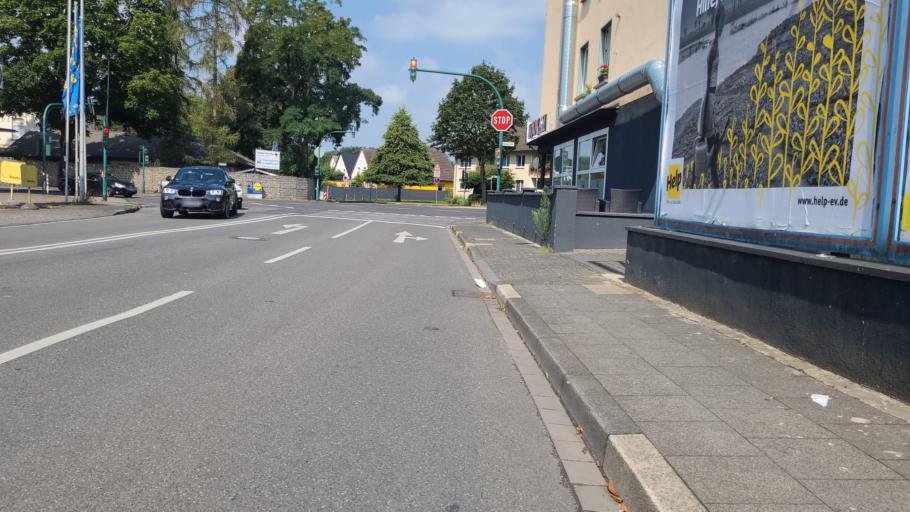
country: DE
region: North Rhine-Westphalia
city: Opladen
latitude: 51.0566
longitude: 7.0024
